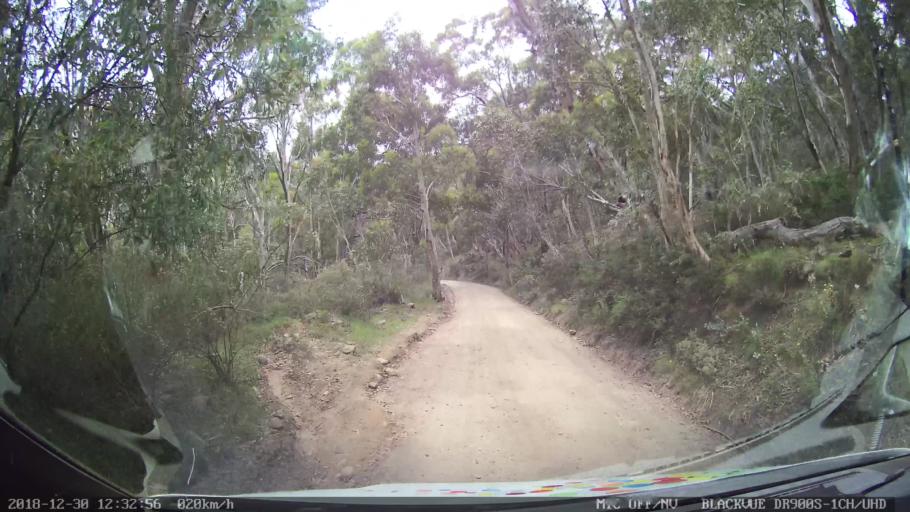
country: AU
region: New South Wales
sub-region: Snowy River
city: Jindabyne
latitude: -36.3244
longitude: 148.4673
